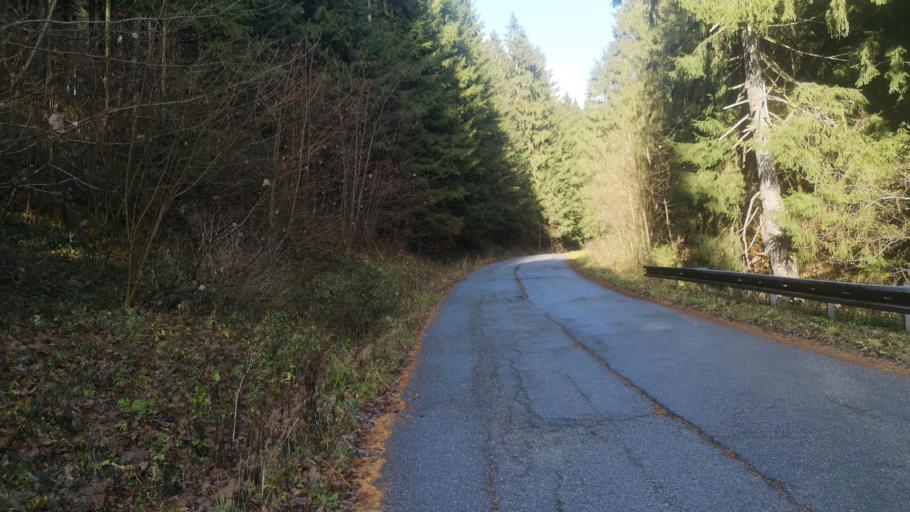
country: SK
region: Banskobystricky
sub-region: Okres Ziar nad Hronom
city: Kremnica
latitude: 48.7608
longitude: 18.9272
